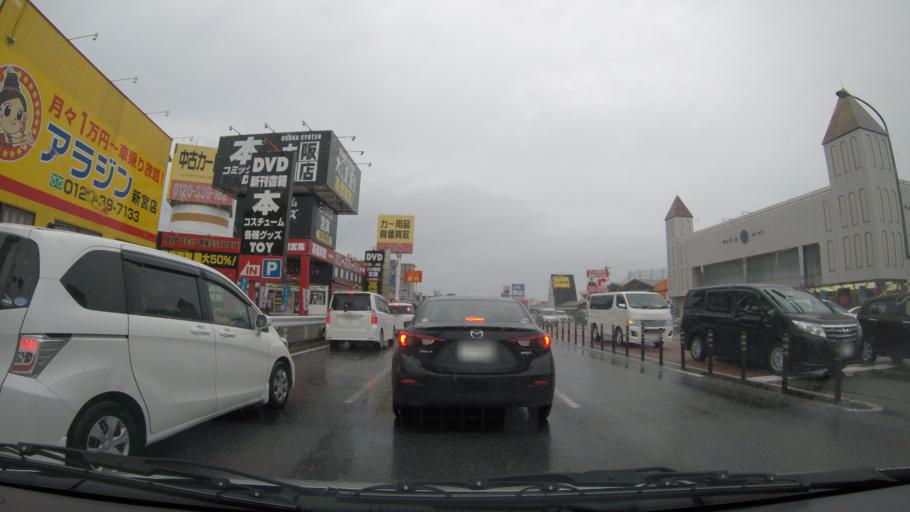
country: JP
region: Fukuoka
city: Shingu
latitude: 33.6913
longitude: 130.4518
